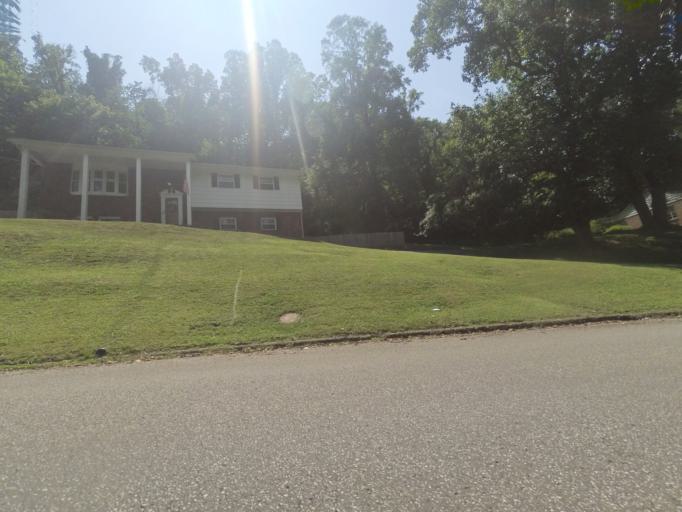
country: US
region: West Virginia
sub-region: Cabell County
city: Huntington
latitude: 38.4020
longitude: -82.4294
